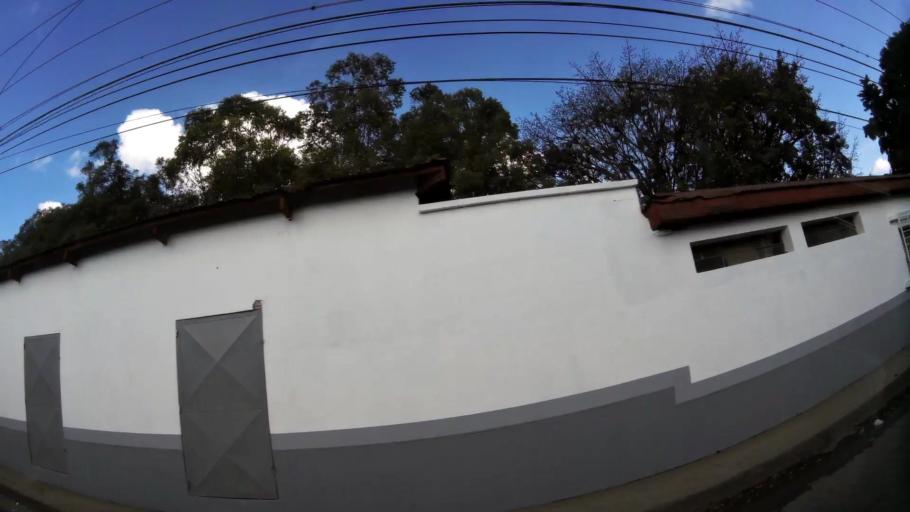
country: GT
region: Guatemala
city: Villa Nueva
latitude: 14.5297
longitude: -90.5899
